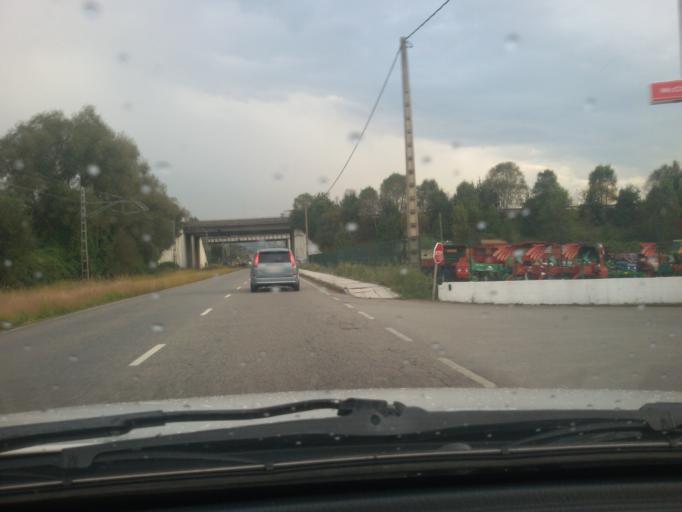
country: ES
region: Asturias
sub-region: Province of Asturias
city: Lugones
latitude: 43.3937
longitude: -5.7888
